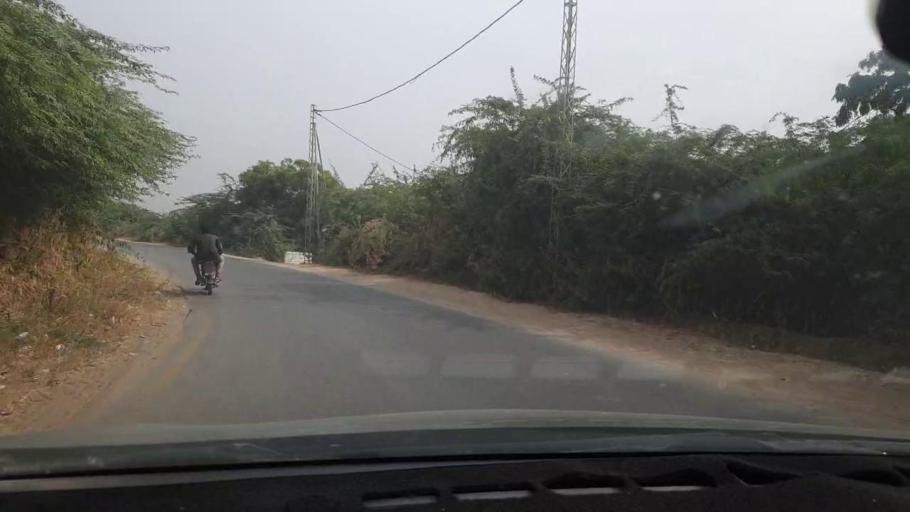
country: PK
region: Sindh
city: Malir Cantonment
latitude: 24.9137
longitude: 67.2624
